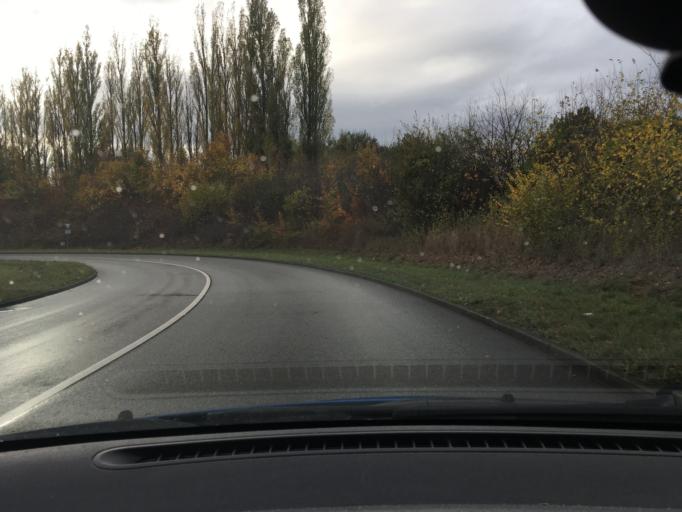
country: DE
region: Schleswig-Holstein
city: Alt Molln
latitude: 53.6235
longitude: 10.6652
